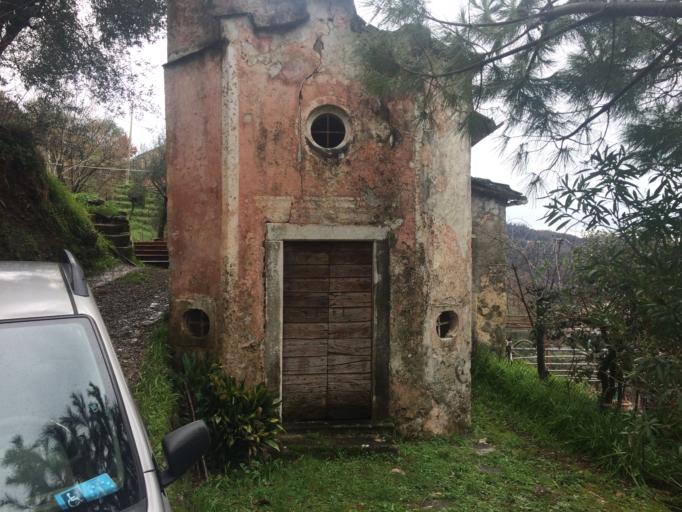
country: IT
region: Tuscany
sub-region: Provincia di Massa-Carrara
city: Carrara
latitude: 44.0849
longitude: 10.1052
